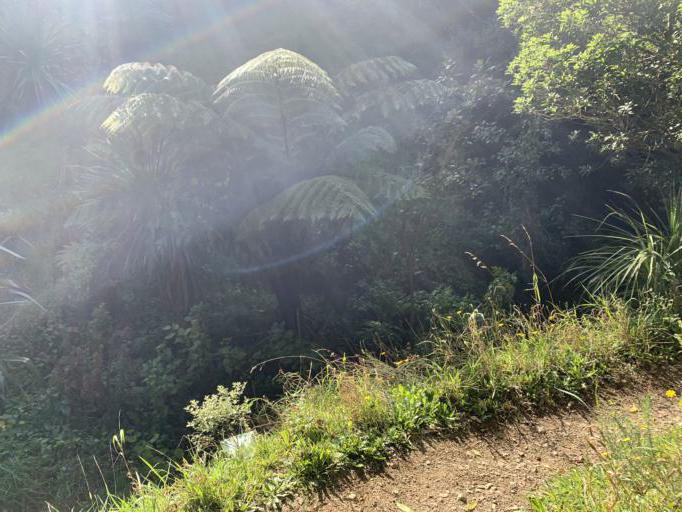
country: NZ
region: Wellington
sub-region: Wellington City
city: Kelburn
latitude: -41.2964
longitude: 174.7554
